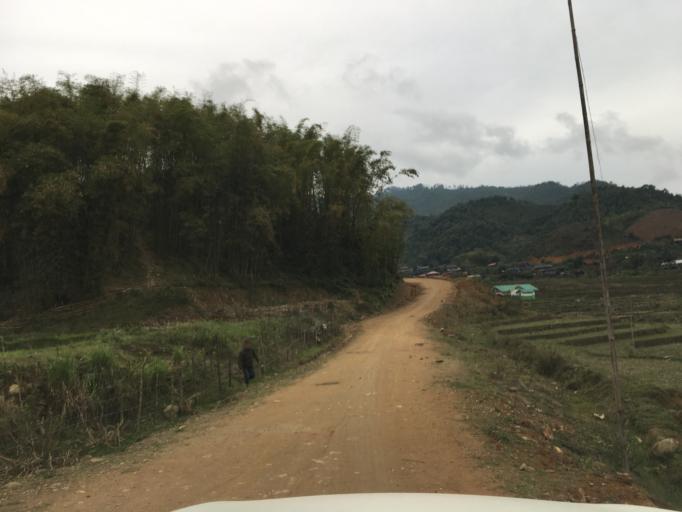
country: VN
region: Thanh Hoa
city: Thi Tran Muong Lat
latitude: 20.4368
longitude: 104.6581
